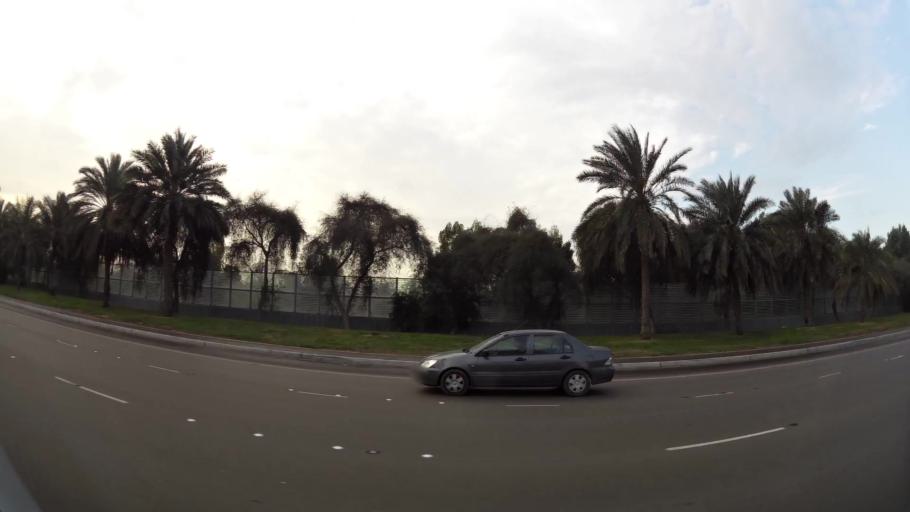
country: AE
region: Abu Dhabi
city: Abu Dhabi
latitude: 24.3961
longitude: 54.5119
